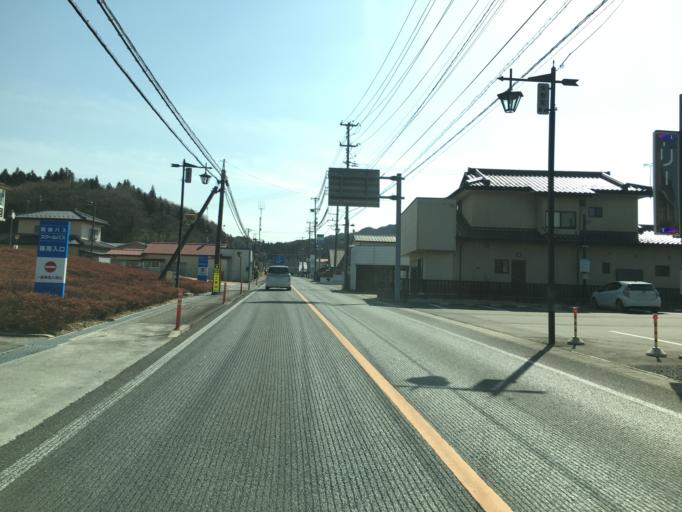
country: JP
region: Ibaraki
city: Daigo
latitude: 36.8686
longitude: 140.4246
